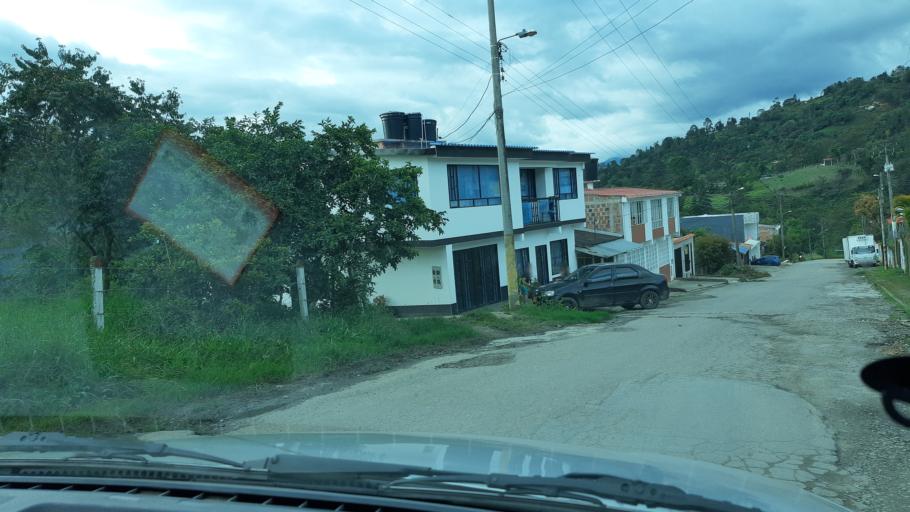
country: CO
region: Boyaca
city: Garagoa
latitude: 5.0908
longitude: -73.3638
